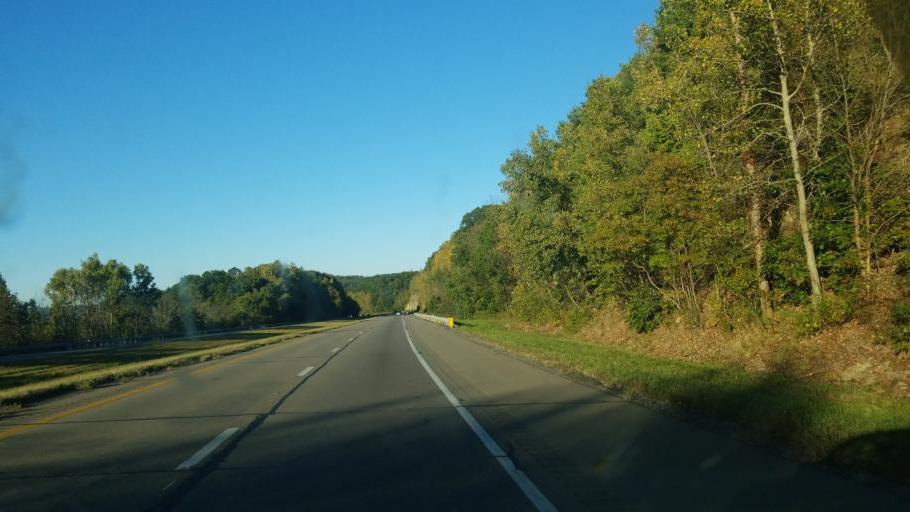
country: US
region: Ohio
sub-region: Tuscarawas County
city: Newcomerstown
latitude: 40.2601
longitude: -81.5504
